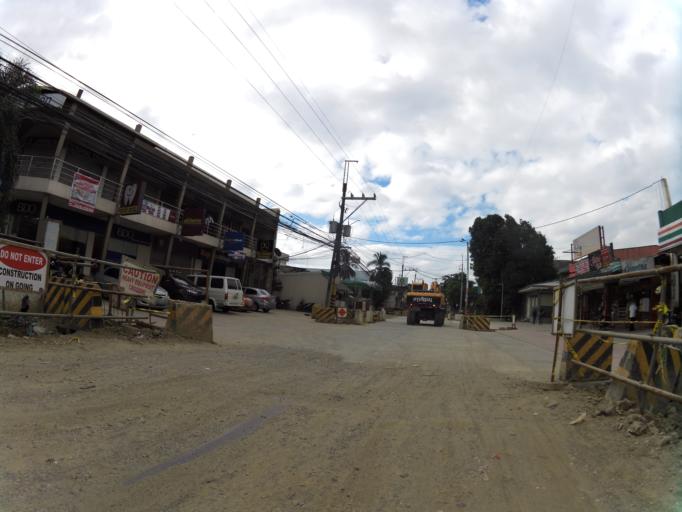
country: PH
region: Calabarzon
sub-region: Province of Rizal
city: Antipolo
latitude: 14.6421
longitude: 121.1105
